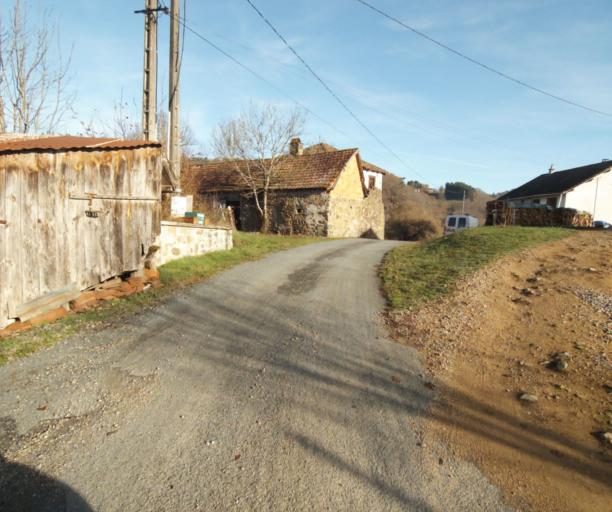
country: FR
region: Limousin
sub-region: Departement de la Correze
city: Laguenne
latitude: 45.2481
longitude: 1.7878
